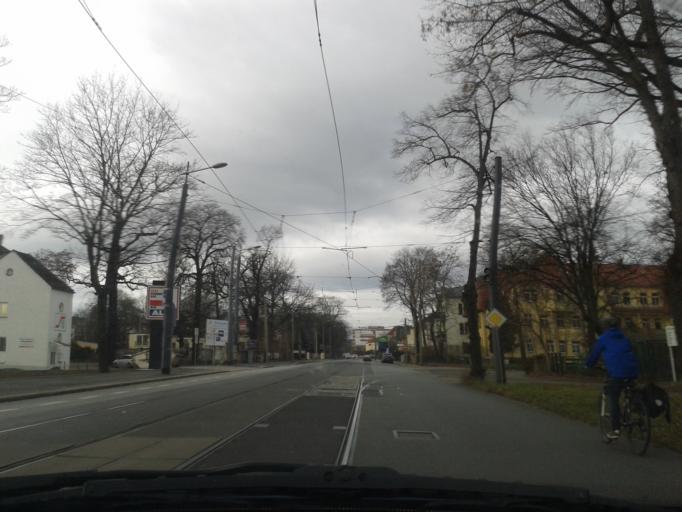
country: DE
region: Saxony
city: Radebeul
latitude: 51.0992
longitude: 13.6888
